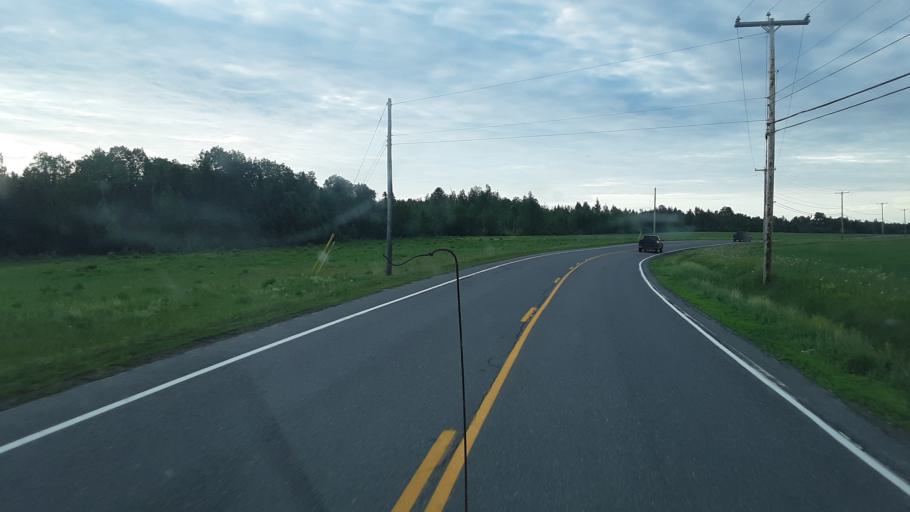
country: US
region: Maine
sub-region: Aroostook County
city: Presque Isle
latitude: 46.5444
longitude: -68.3660
